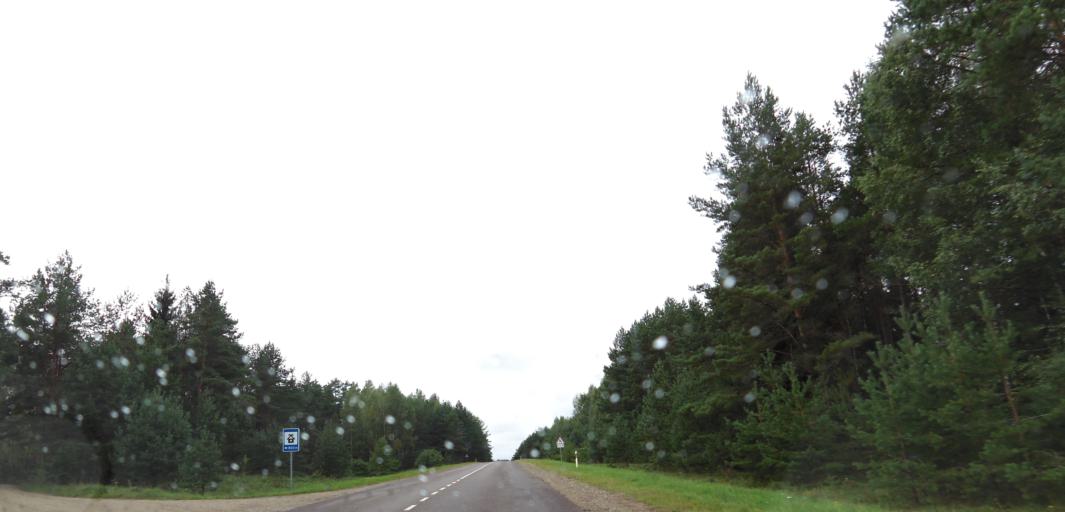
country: LT
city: Moletai
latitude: 55.2141
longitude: 25.3606
